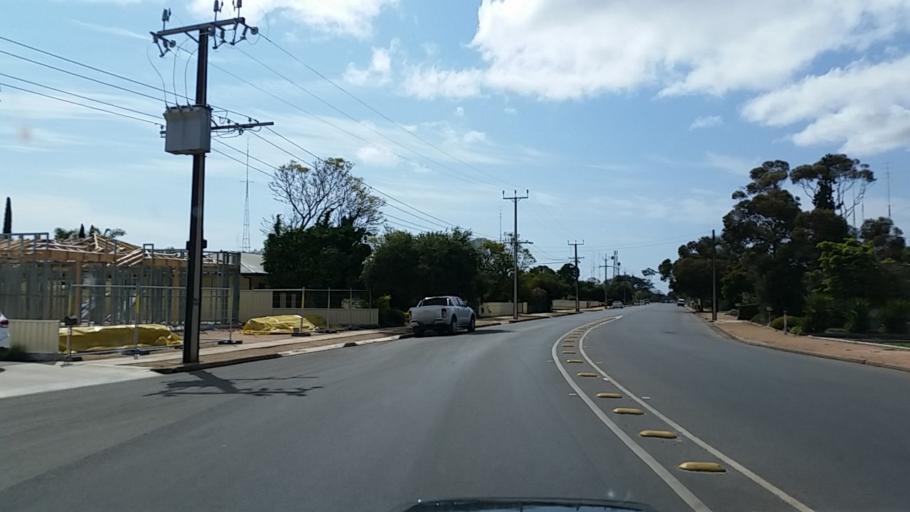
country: AU
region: South Australia
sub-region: Port Pirie City and Dists
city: Port Pirie
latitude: -33.2030
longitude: 138.0103
